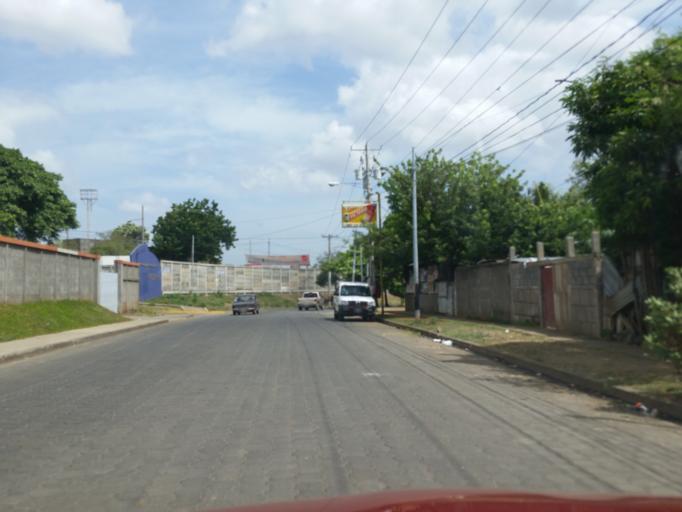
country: NI
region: Managua
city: Managua
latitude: 12.1320
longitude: -86.2832
